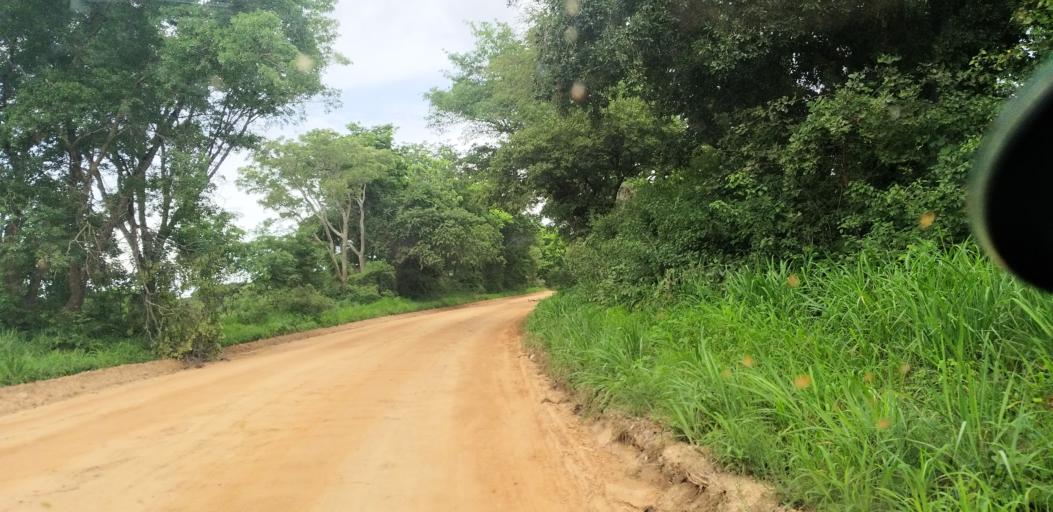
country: ZM
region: Lusaka
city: Lusaka
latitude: -15.1882
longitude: 28.4458
